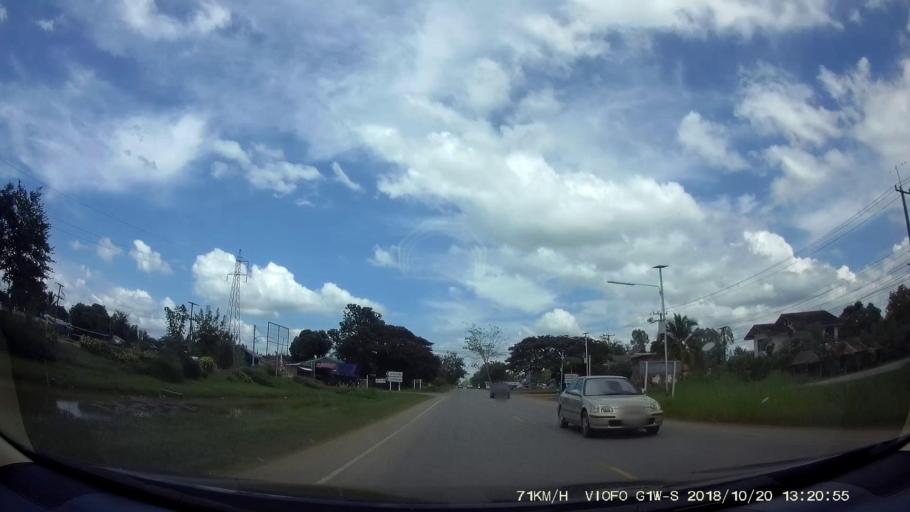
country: TH
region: Chaiyaphum
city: Khon San
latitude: 16.5532
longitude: 101.9066
